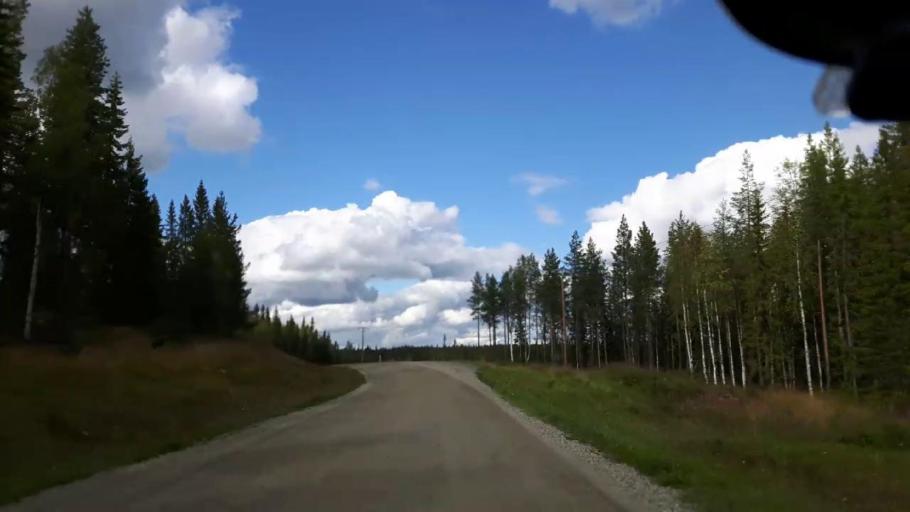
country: SE
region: Jaemtland
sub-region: Stroemsunds Kommun
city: Stroemsund
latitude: 63.3797
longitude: 15.5623
